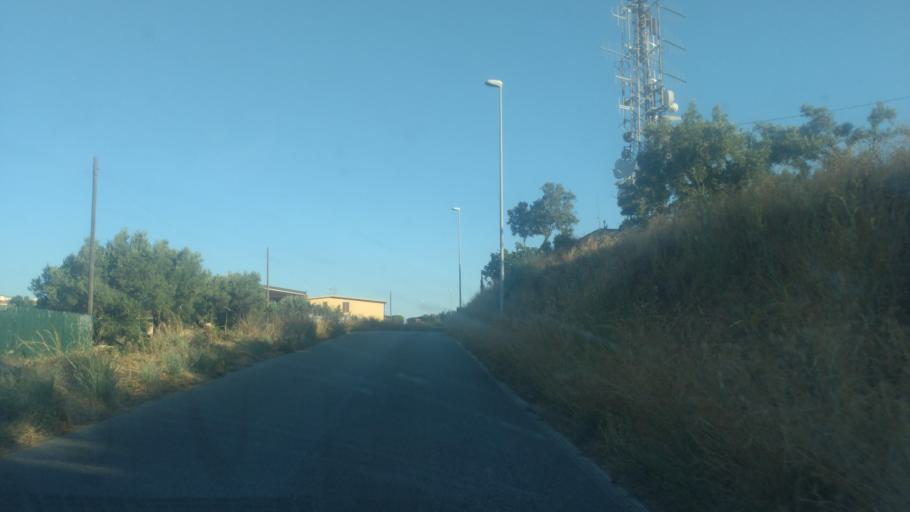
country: IT
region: Calabria
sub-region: Provincia di Catanzaro
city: Staletti
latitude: 38.7632
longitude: 16.5565
